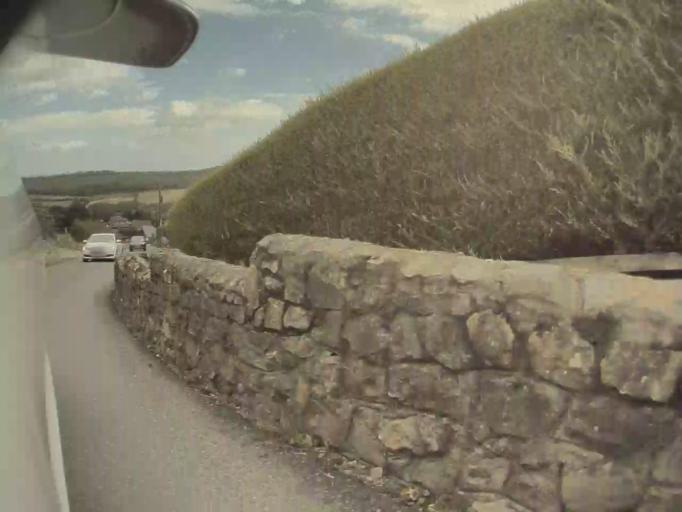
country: IE
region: Leinster
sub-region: Wicklow
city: Kilmacanoge
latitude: 53.1450
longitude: -6.1403
